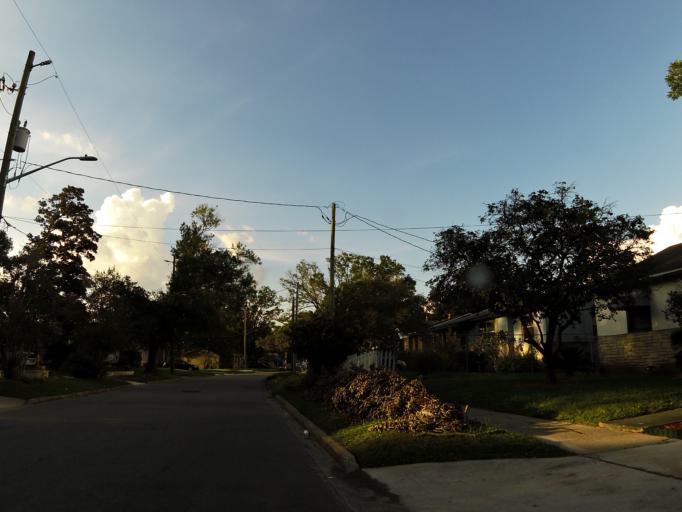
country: US
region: Florida
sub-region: Duval County
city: Jacksonville
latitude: 30.3455
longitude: -81.6925
